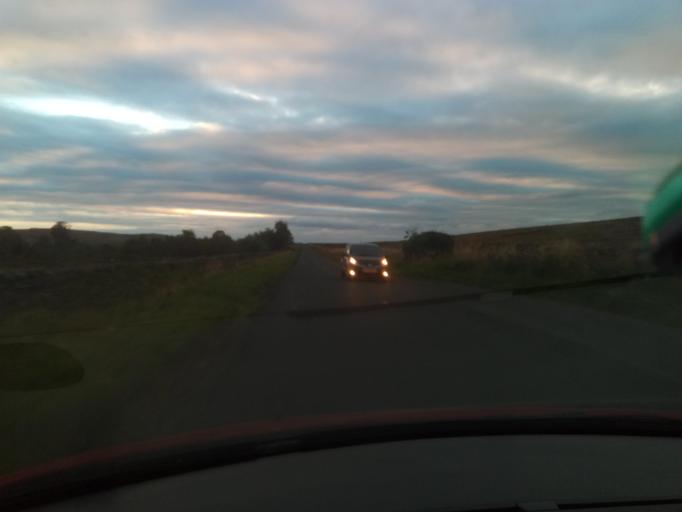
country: GB
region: England
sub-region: Northumberland
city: Bardon Mill
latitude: 54.9275
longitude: -2.3668
